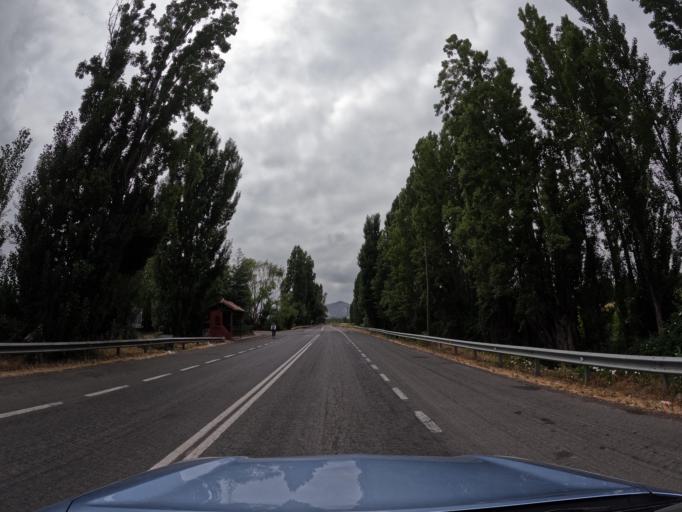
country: CL
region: Maule
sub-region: Provincia de Curico
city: Teno
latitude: -34.7518
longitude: -71.2199
